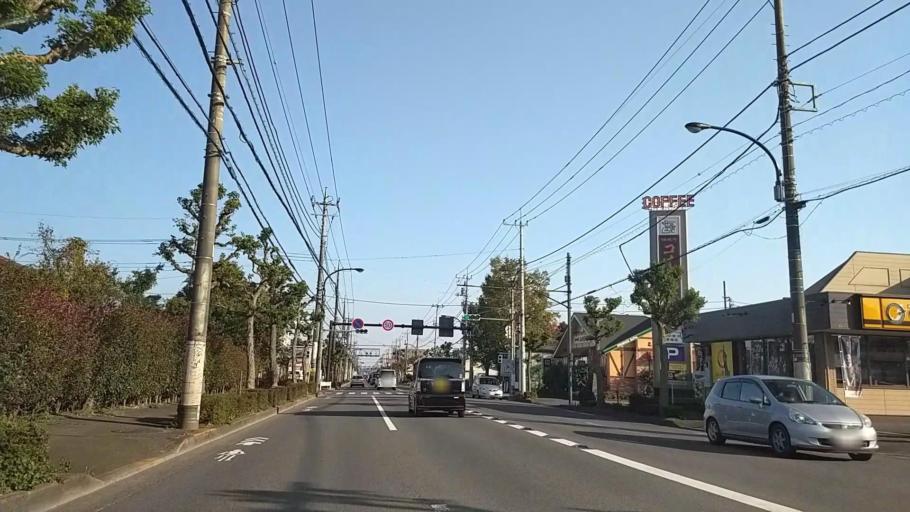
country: JP
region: Tokyo
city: Fussa
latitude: 35.7844
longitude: 139.3129
